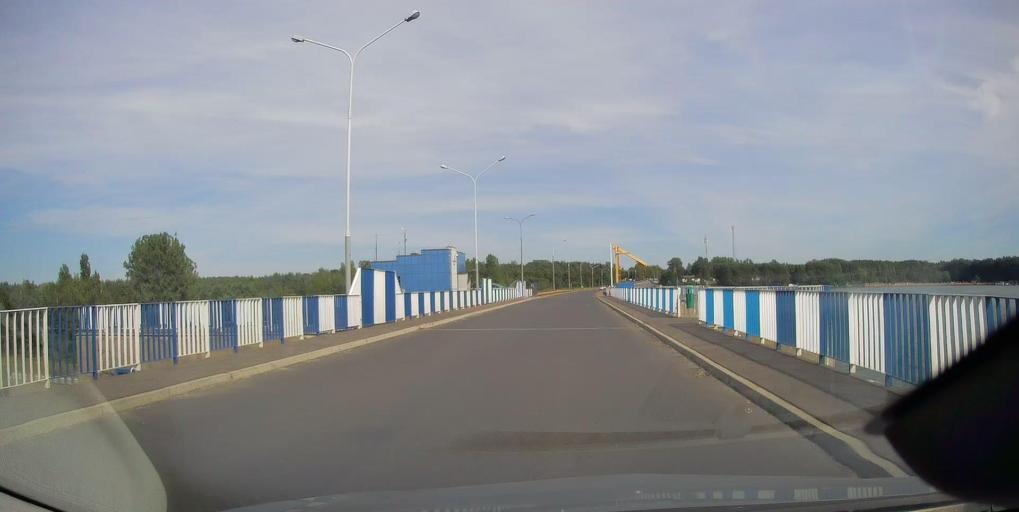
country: PL
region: Lodz Voivodeship
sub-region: Powiat tomaszowski
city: Tomaszow Mazowiecki
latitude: 51.4740
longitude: 20.0058
